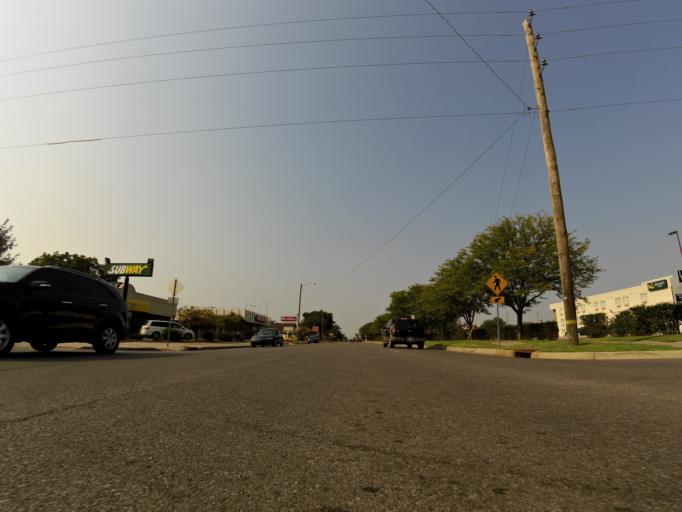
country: US
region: Kansas
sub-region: Sedgwick County
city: Wichita
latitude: 37.7001
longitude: -97.3356
